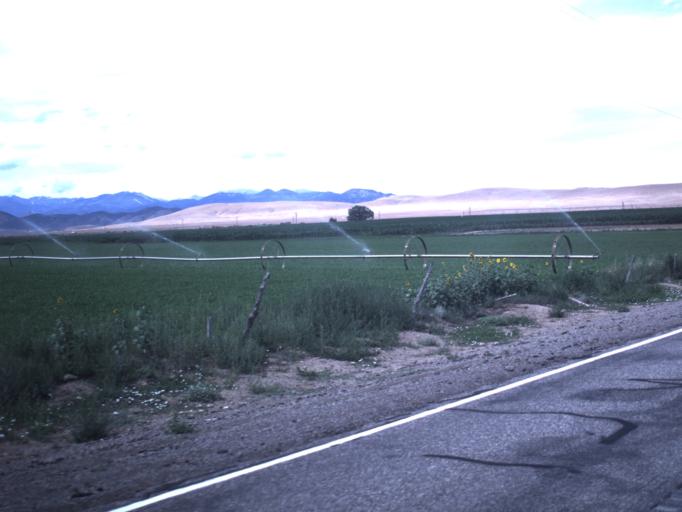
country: US
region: Utah
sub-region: Sevier County
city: Monroe
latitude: 38.6290
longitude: -112.1510
